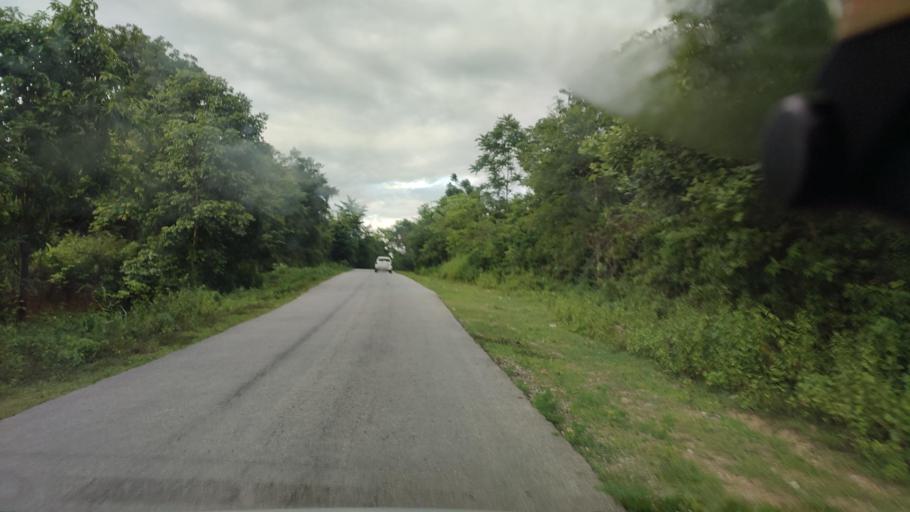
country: MM
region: Mandalay
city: Nay Pyi Taw
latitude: 19.9925
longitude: 95.9382
